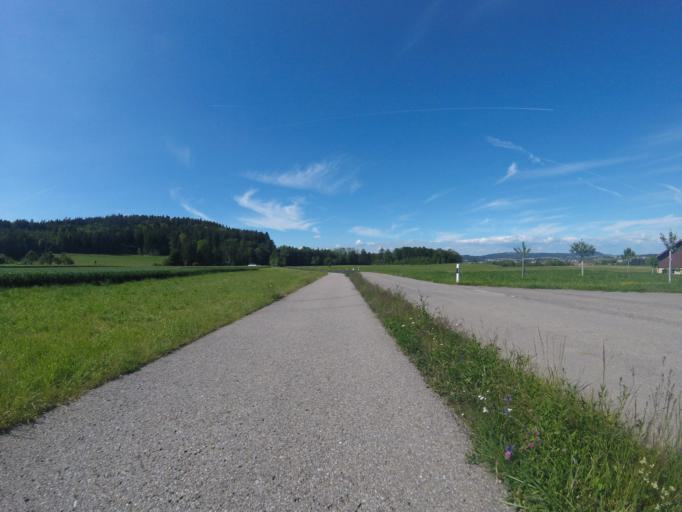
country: CH
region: Saint Gallen
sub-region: Wahlkreis Wil
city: Jonschwil
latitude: 47.4271
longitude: 9.0619
